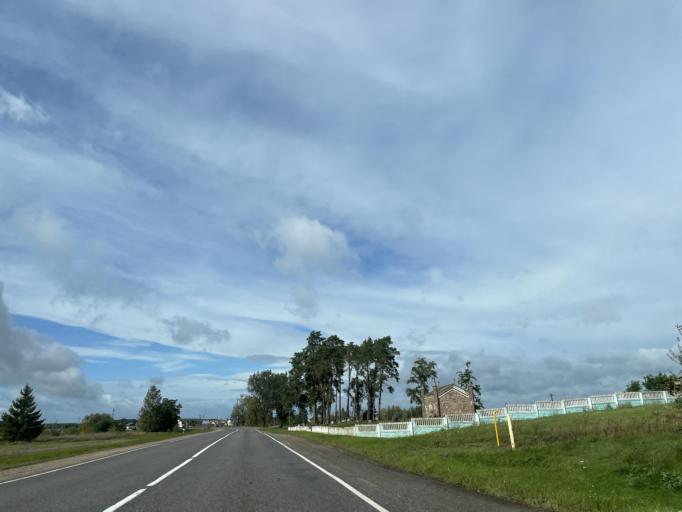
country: BY
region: Brest
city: Kosava
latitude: 52.7467
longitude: 25.1754
